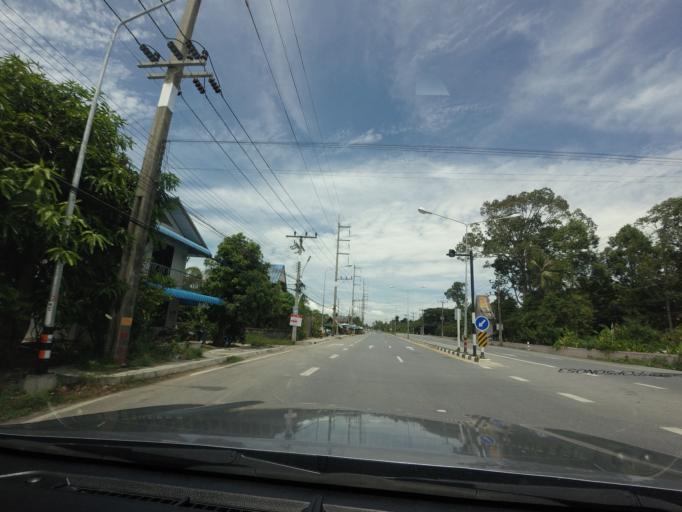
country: TH
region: Songkhla
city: Krasae Sin
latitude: 7.6132
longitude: 100.3978
